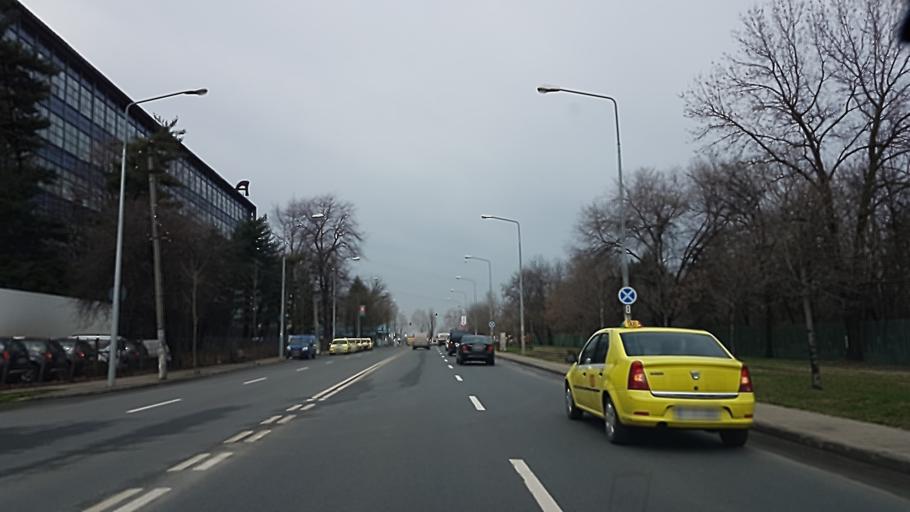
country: RO
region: Ilfov
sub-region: Comuna Pantelimon
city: Pantelimon
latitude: 44.4394
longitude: 26.1945
